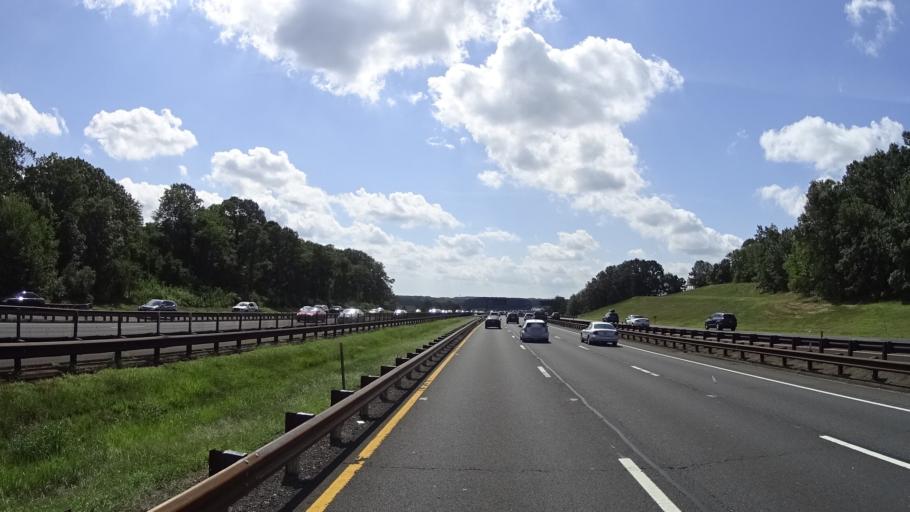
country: US
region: New Jersey
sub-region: Middlesex County
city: South Amboy
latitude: 40.4570
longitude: -74.2759
